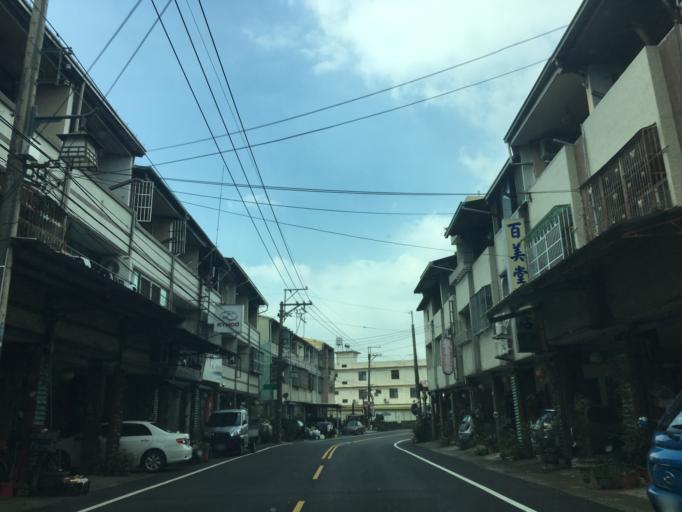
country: TW
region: Taiwan
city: Fengyuan
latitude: 24.2218
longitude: 120.7939
